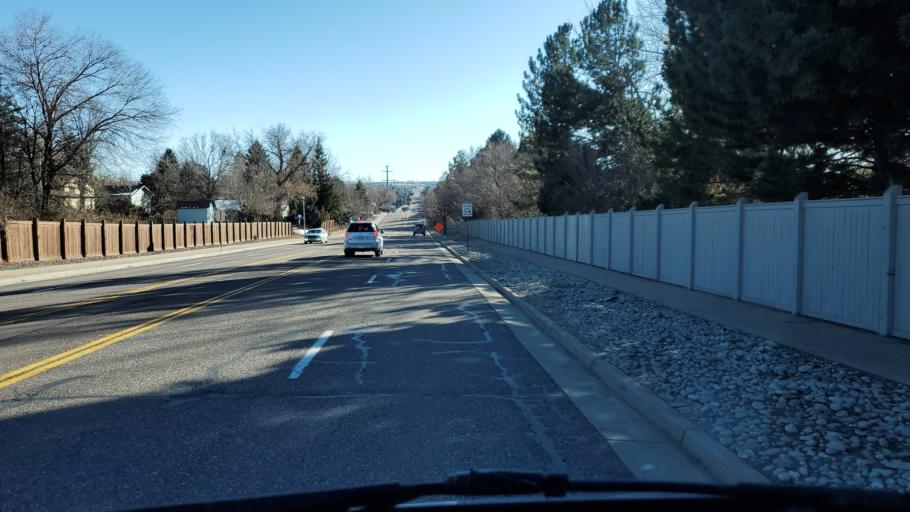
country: US
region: Colorado
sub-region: Arapahoe County
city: Castlewood
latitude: 39.5842
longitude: -104.9043
